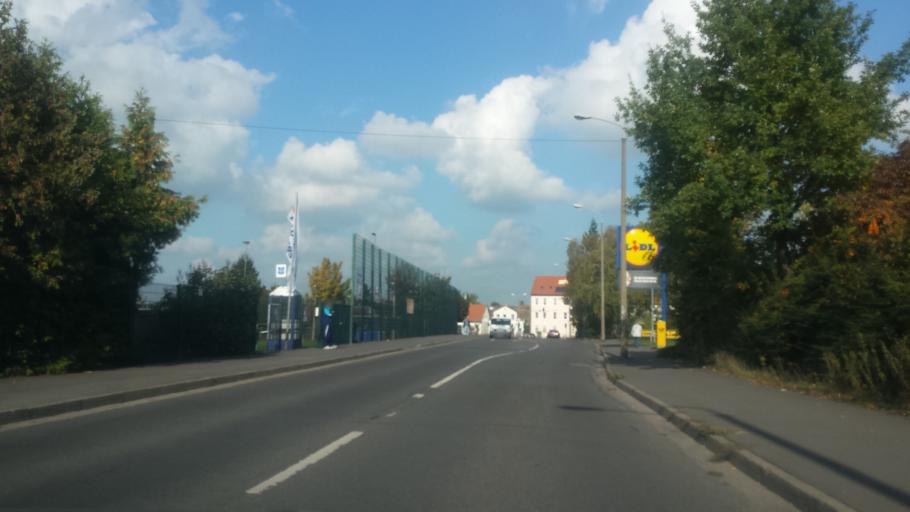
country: DE
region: Saxony
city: Taucha
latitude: 51.3779
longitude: 12.4301
